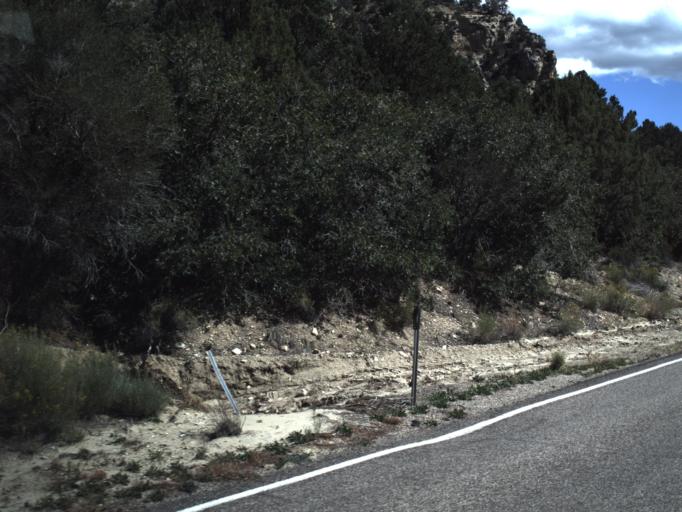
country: US
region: Utah
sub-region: Iron County
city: Cedar City
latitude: 37.6453
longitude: -112.9673
